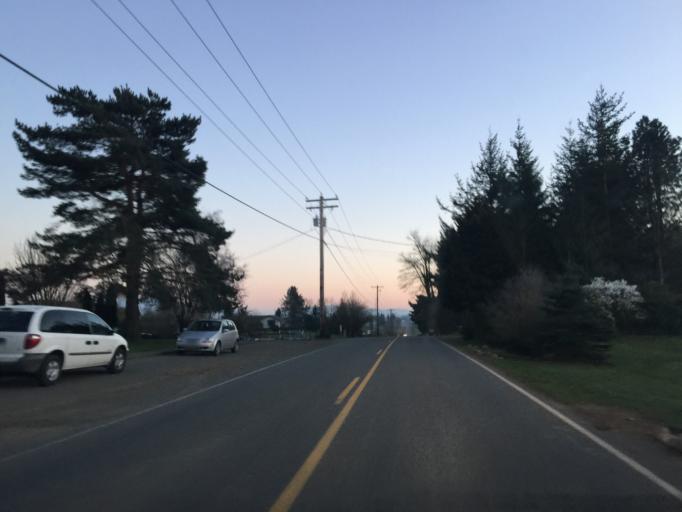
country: US
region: Washington
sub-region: Whatcom County
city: Lynden
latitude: 48.9603
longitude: -122.4076
